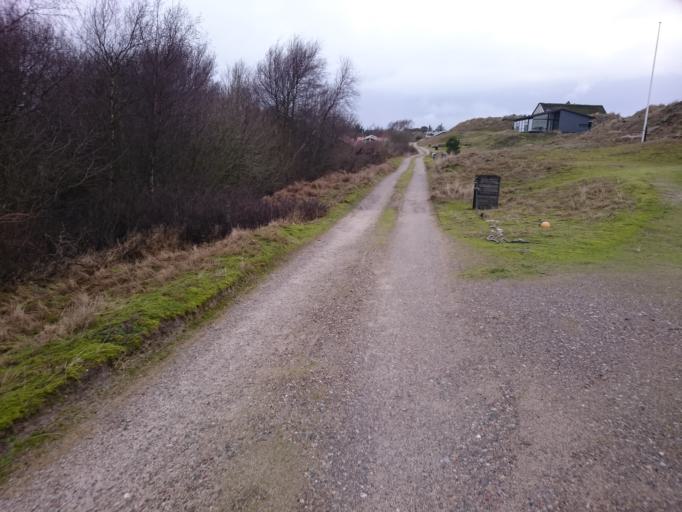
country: DK
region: South Denmark
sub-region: Fano Kommune
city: Nordby
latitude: 55.4345
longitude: 8.3794
